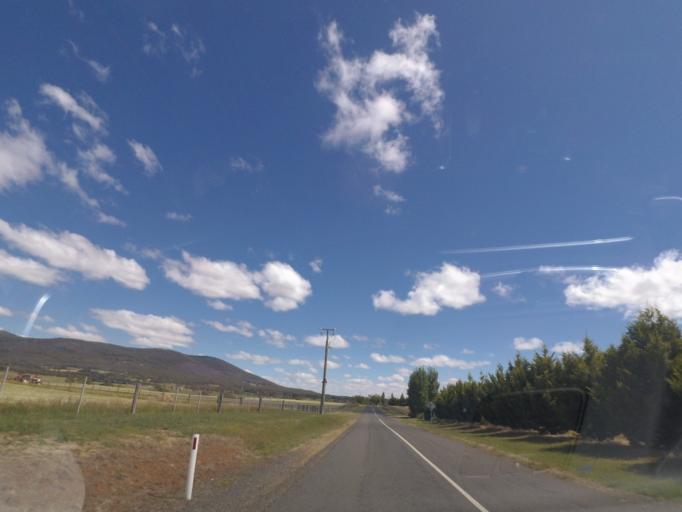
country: AU
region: Victoria
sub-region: Hume
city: Sunbury
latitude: -37.3353
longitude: 144.5582
